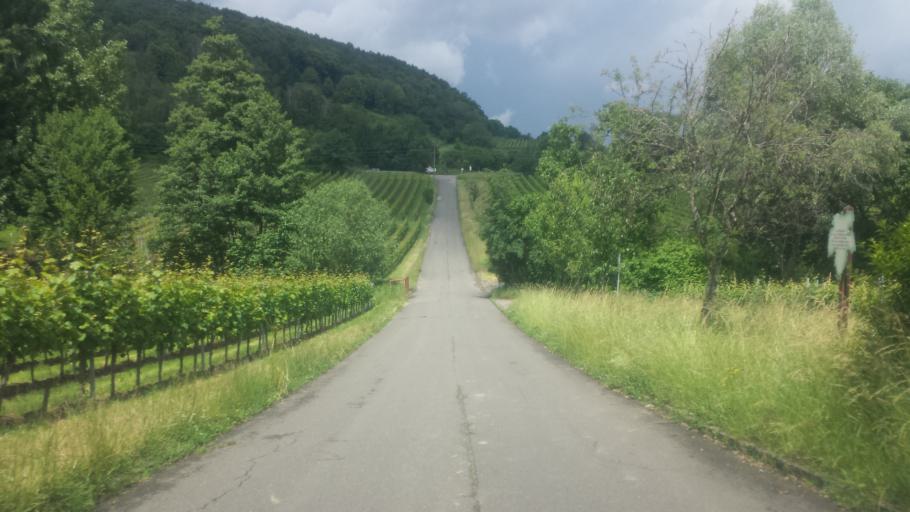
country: DE
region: Rheinland-Pfalz
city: Rhodt unter Rietburg
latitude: 49.2806
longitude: 8.0973
